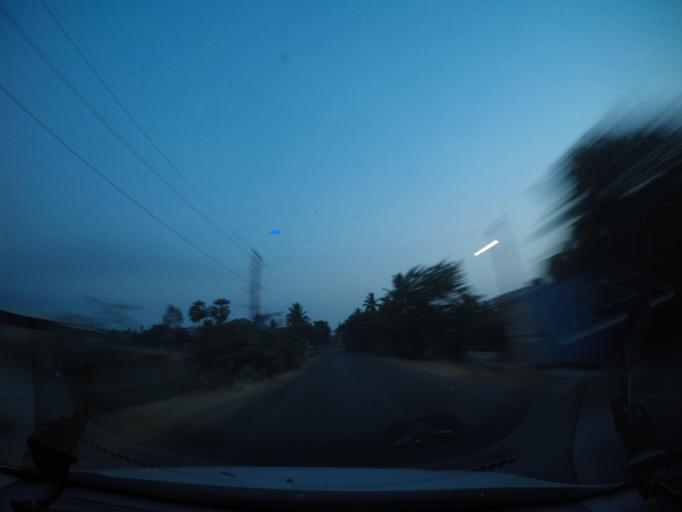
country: IN
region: Andhra Pradesh
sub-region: West Godavari
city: Tadepallegudem
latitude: 16.7791
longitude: 81.4243
